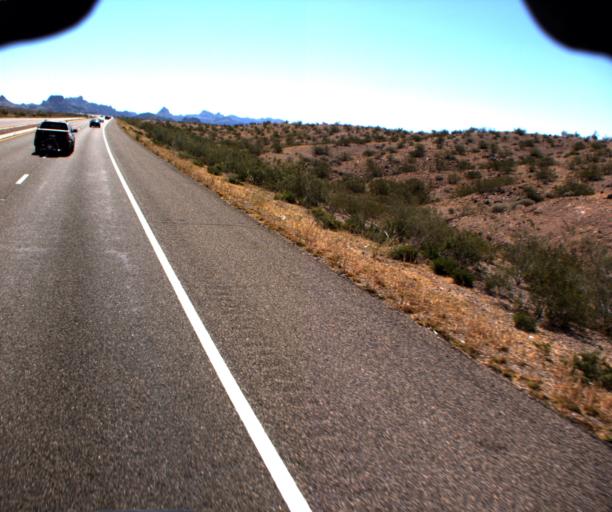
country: US
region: Nevada
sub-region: Clark County
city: Laughlin
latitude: 35.1883
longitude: -114.5086
